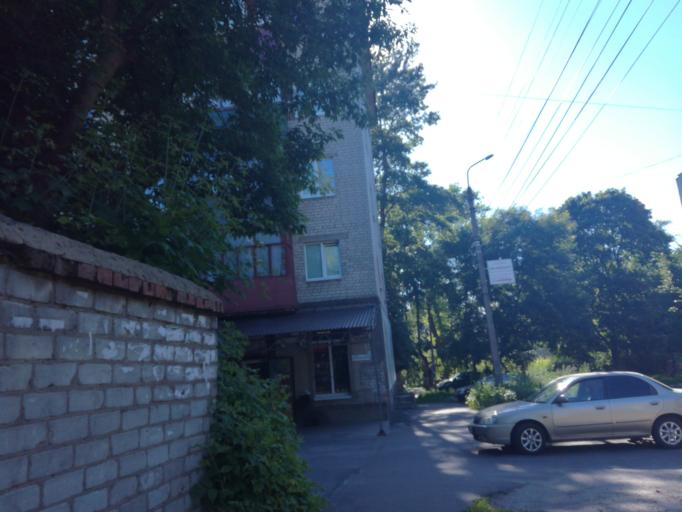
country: RU
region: Kursk
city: Kursk
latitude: 51.7464
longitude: 36.1827
